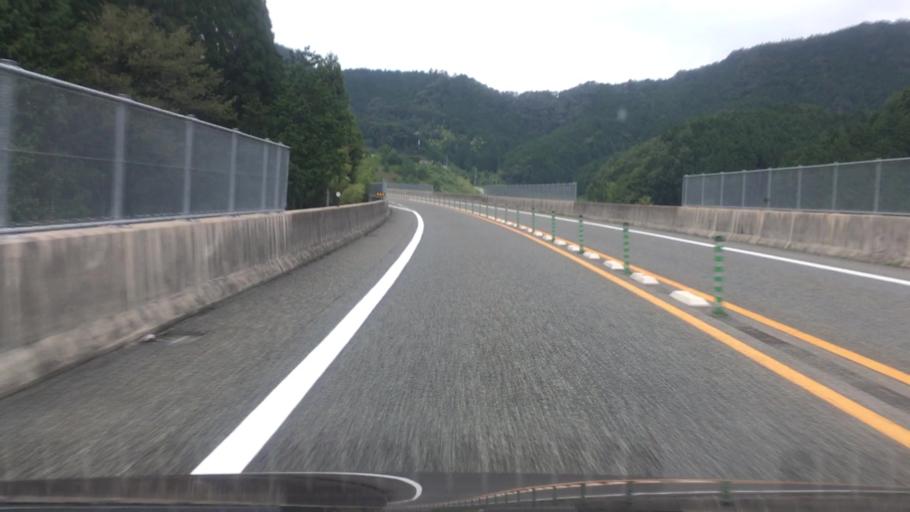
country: JP
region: Hyogo
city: Toyooka
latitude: 35.3090
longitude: 134.8758
